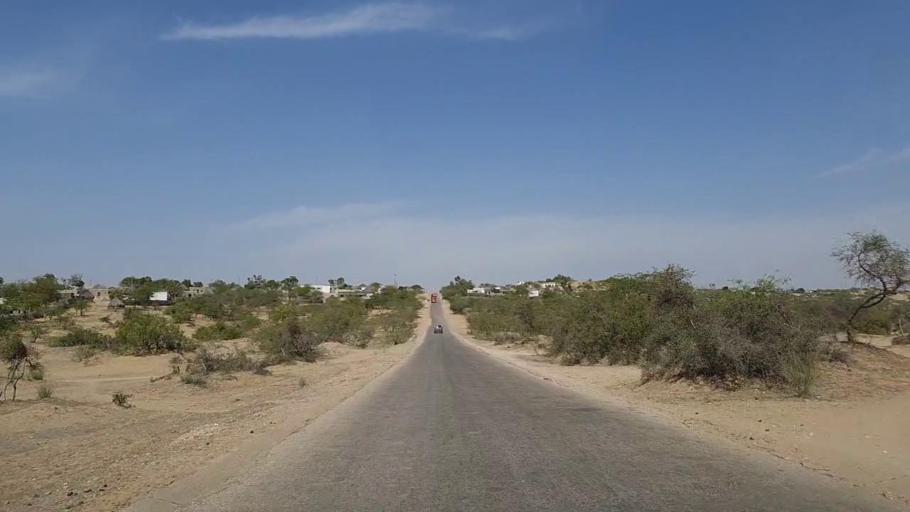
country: PK
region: Sindh
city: Mithi
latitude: 24.9855
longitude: 69.9225
